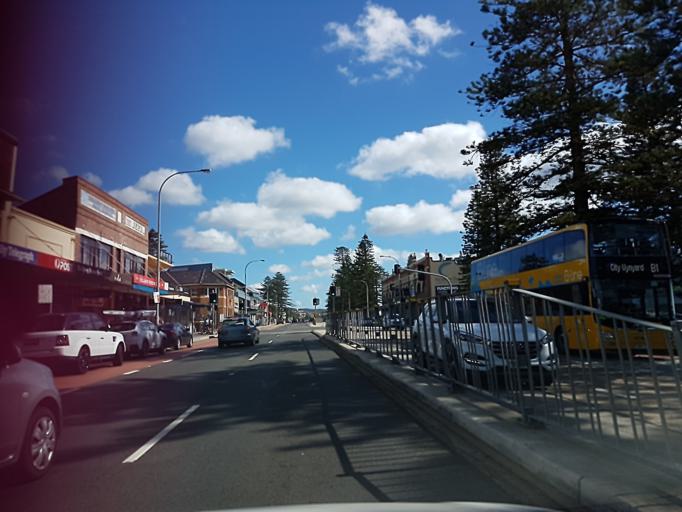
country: AU
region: New South Wales
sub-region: Warringah
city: Dee Why
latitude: -33.7326
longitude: 151.3015
